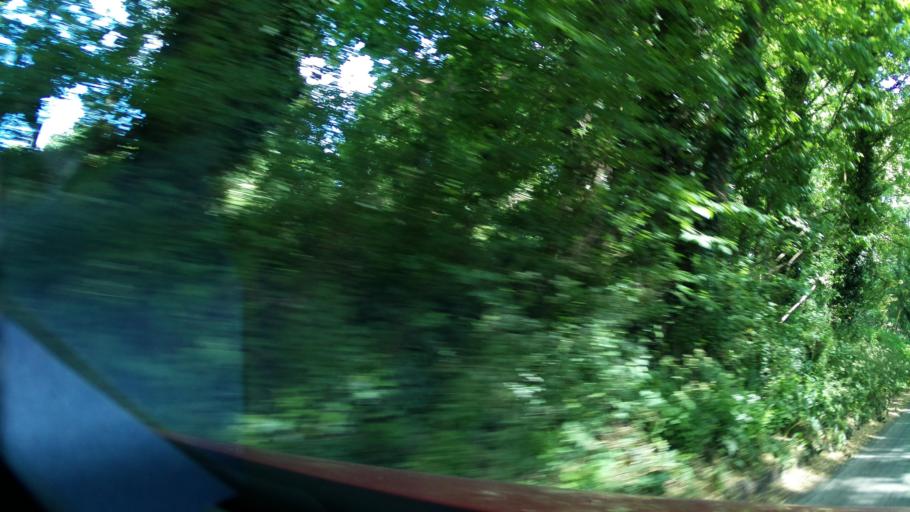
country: GB
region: England
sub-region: Wiltshire
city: Rushall
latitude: 51.2702
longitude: -1.8036
